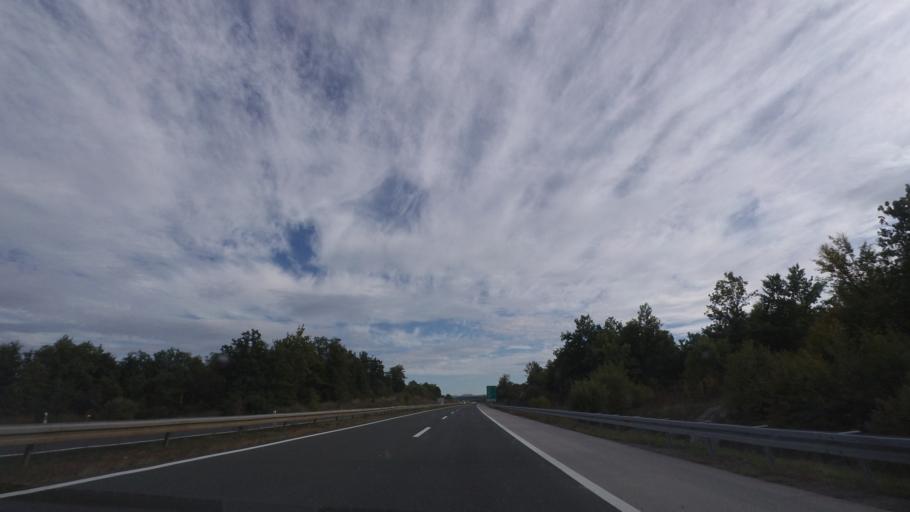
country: HR
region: Zadarska
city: Starigrad
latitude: 44.4500
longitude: 15.6136
